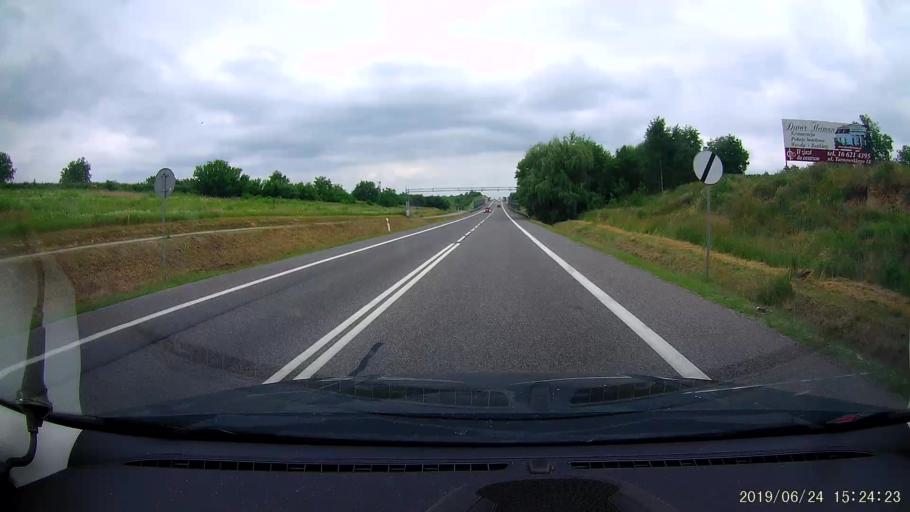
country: PL
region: Subcarpathian Voivodeship
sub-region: Powiat jaroslawski
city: Jaroslaw
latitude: 50.0295
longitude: 22.6520
